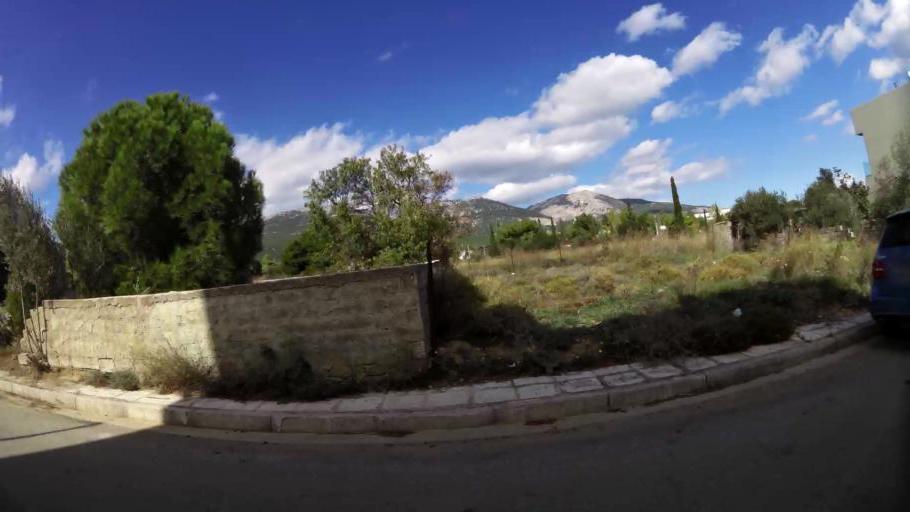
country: GR
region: Attica
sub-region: Nomarchia Anatolikis Attikis
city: Thrakomakedones
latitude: 38.1106
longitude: 23.7416
